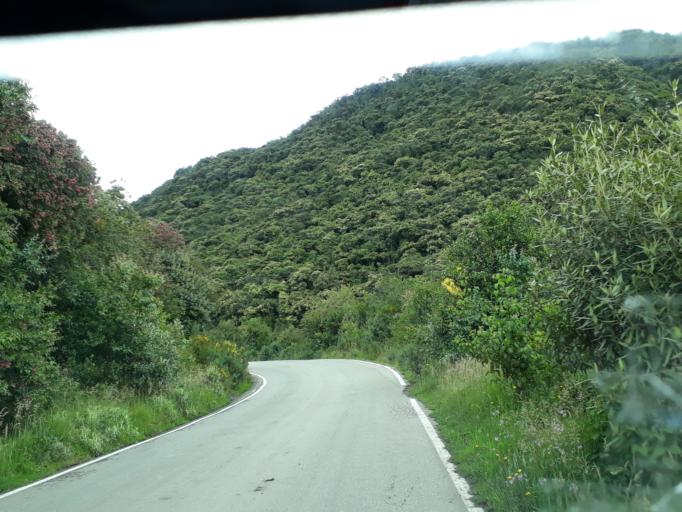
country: CO
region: Cundinamarca
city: La Mesa
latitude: 5.2061
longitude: -73.9041
